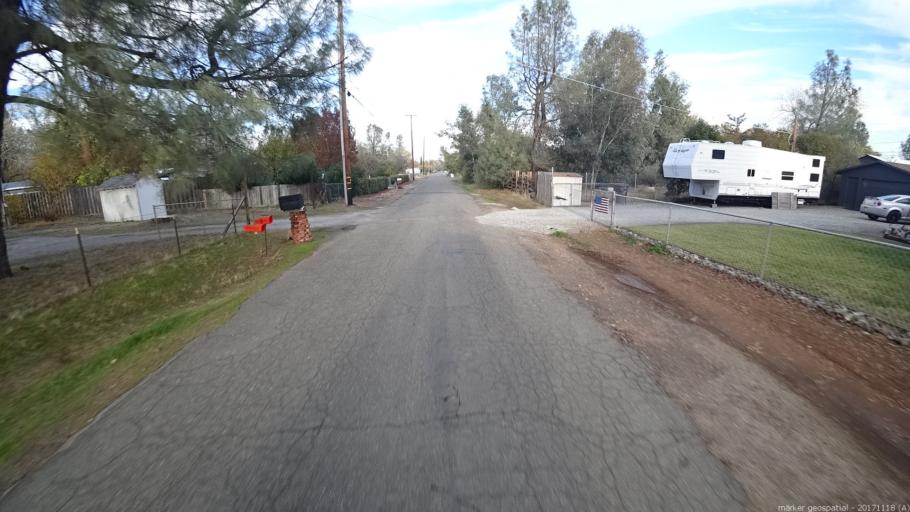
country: US
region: California
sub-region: Shasta County
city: Anderson
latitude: 40.4604
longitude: -122.3350
